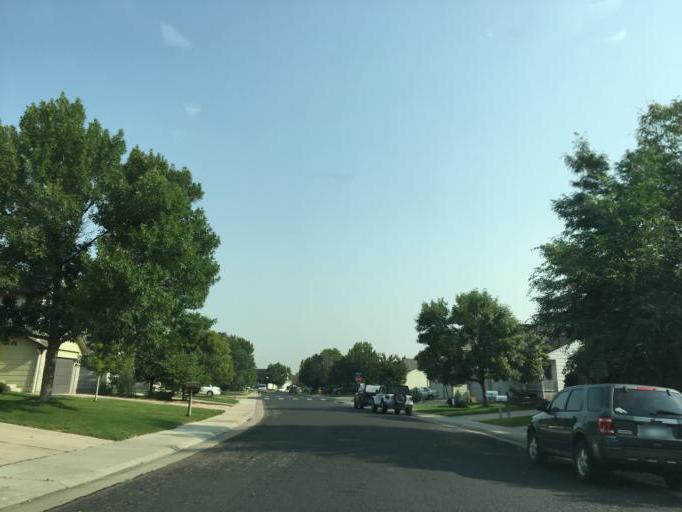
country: US
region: Colorado
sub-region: Adams County
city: Todd Creek
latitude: 39.9051
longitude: -104.8536
